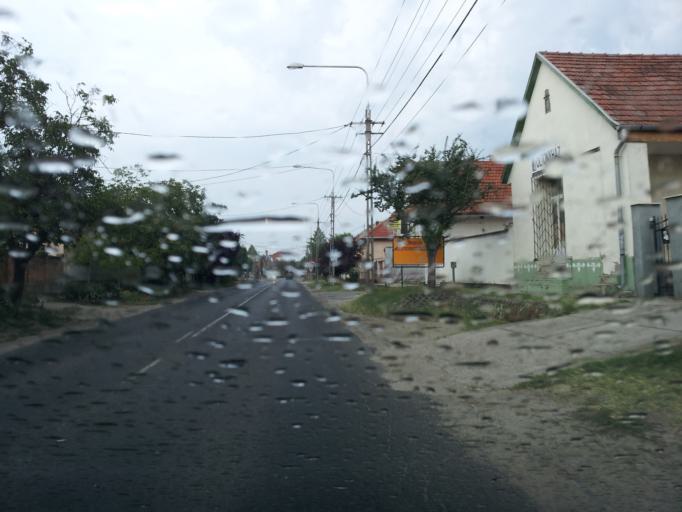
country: HU
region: Pest
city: Taksony
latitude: 47.3307
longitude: 19.0621
